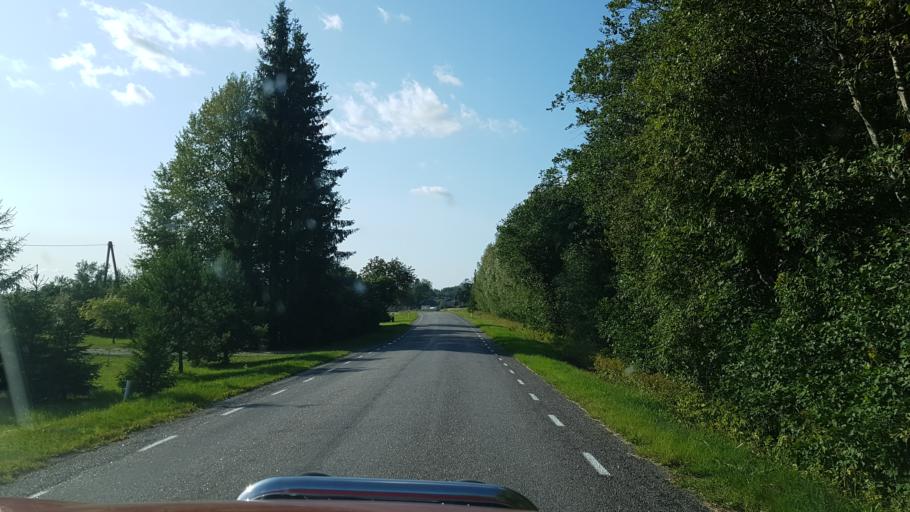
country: EE
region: Jaervamaa
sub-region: Jaerva-Jaani vald
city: Jarva-Jaani
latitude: 59.1129
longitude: 25.6694
